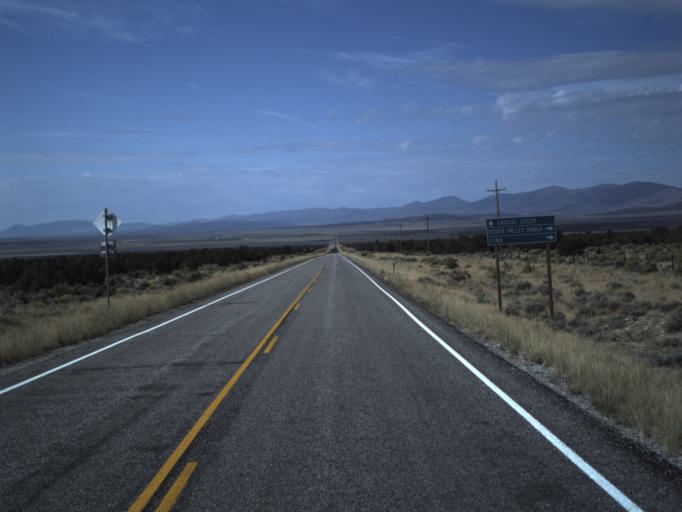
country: US
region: Idaho
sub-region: Cassia County
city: Burley
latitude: 41.8186
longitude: -113.4311
